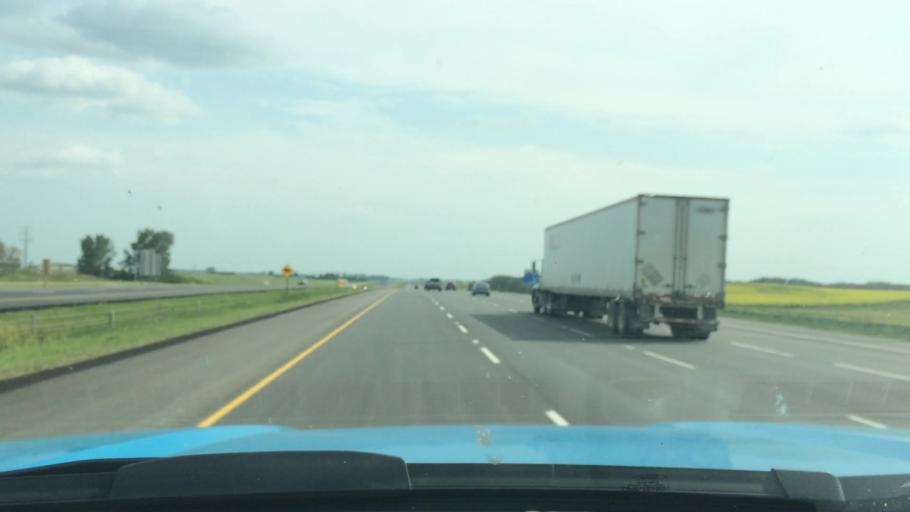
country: CA
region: Alberta
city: Crossfield
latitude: 51.3819
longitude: -114.0020
